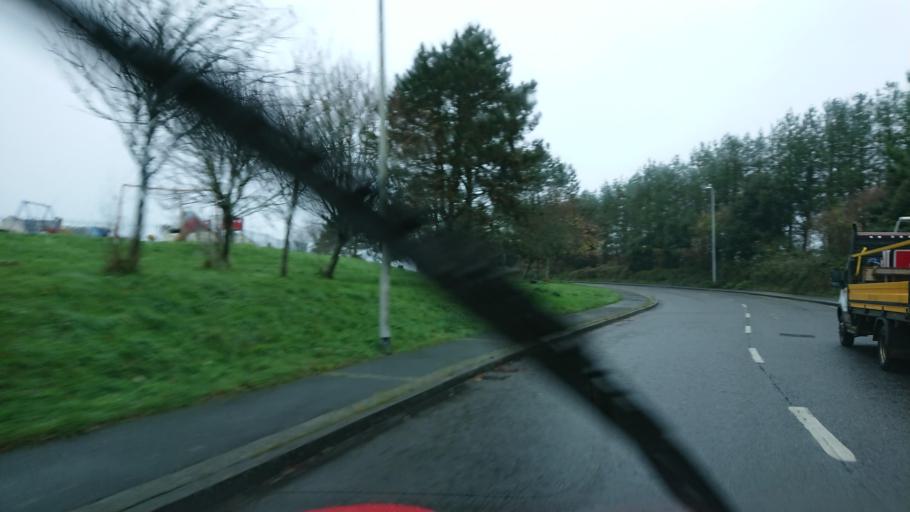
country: GB
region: England
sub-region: Plymouth
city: Plymouth
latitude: 50.3571
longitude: -4.1204
